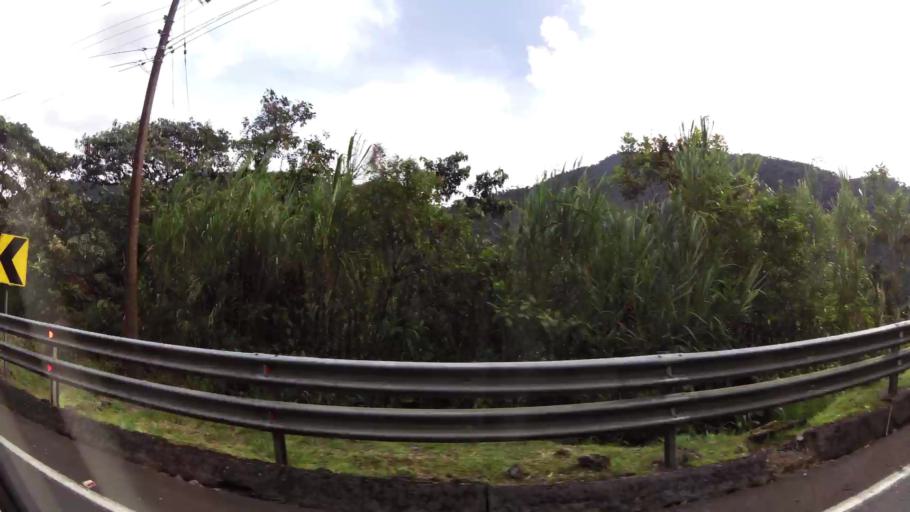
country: EC
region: Pastaza
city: Puyo
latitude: -1.4493
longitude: -78.1728
